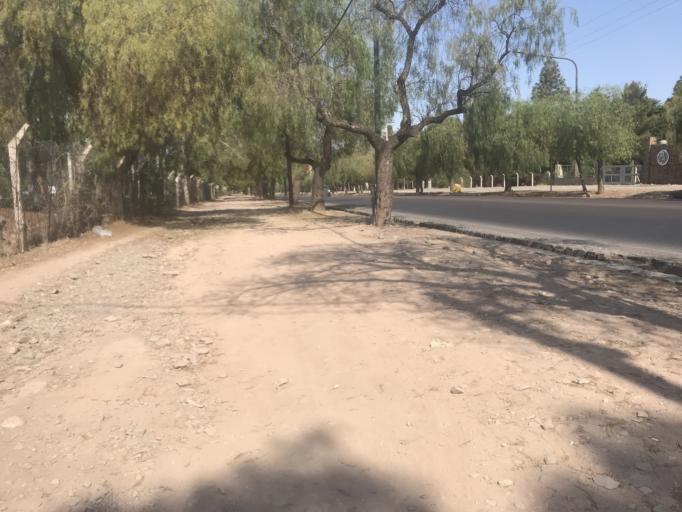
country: AR
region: Mendoza
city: Mendoza
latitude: -32.8831
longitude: -68.8793
